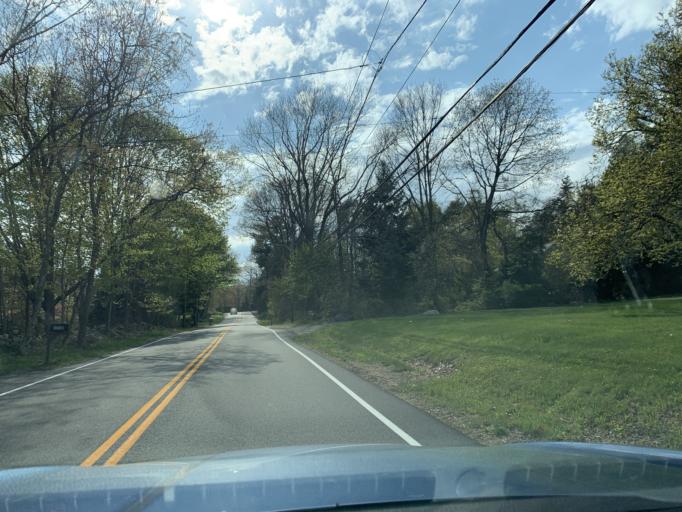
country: US
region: Rhode Island
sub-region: Washington County
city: Exeter
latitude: 41.5942
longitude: -71.5162
